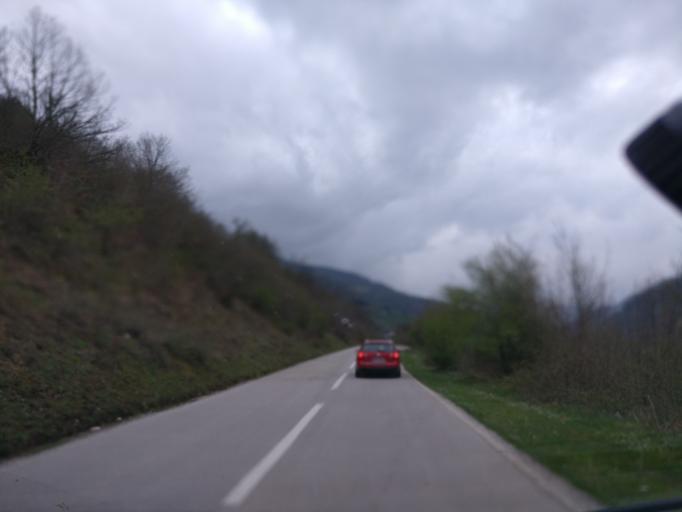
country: BA
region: Republika Srpska
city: Foca
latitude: 43.4440
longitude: 18.7579
